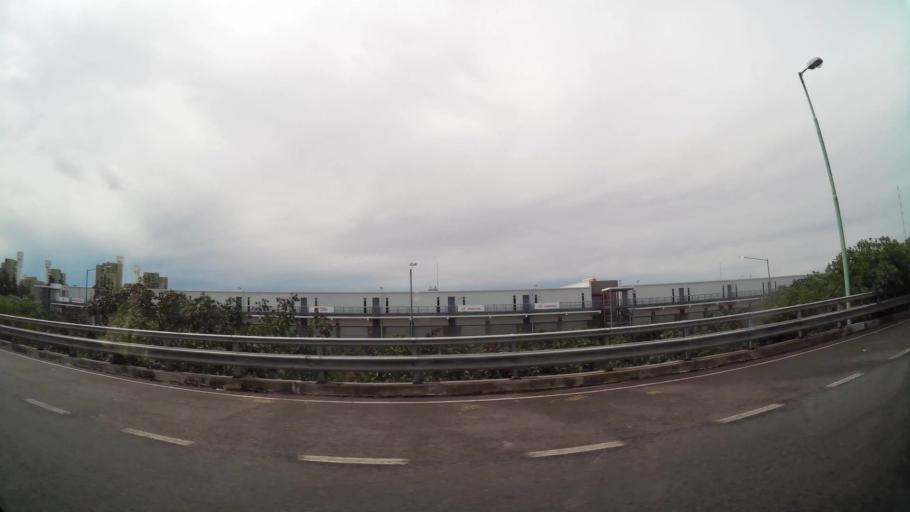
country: AR
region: Buenos Aires F.D.
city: Villa Lugano
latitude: -34.6709
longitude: -58.4417
